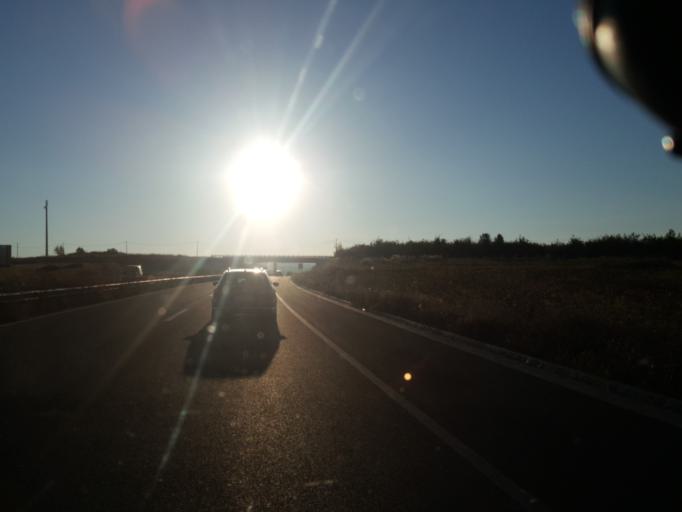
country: XK
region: Prizren
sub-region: Komuna e Malisheves
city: Llazice
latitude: 42.5756
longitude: 20.7190
